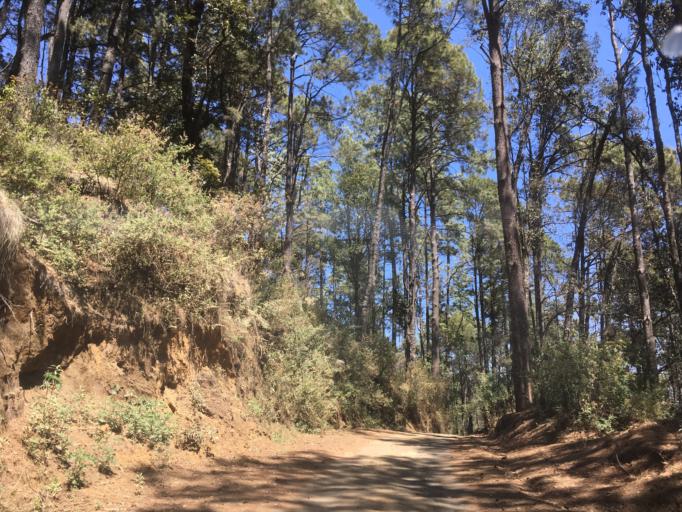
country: MX
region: Michoacan
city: Angahuan
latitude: 19.4701
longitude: -102.2402
